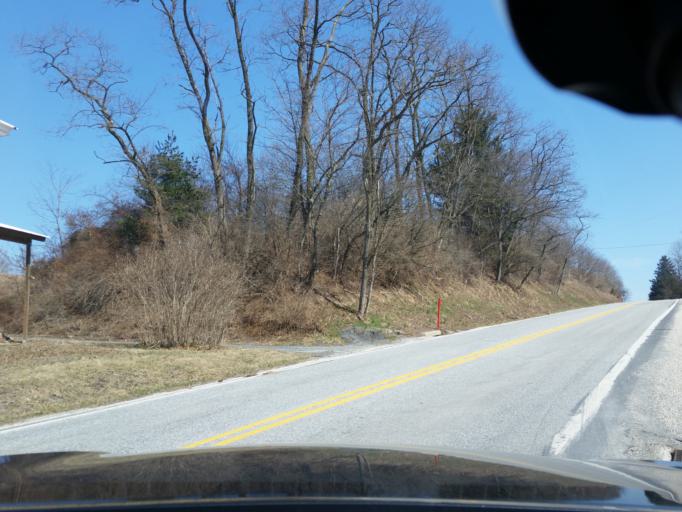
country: US
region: Pennsylvania
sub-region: Cumberland County
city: Schlusser
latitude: 40.3218
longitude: -77.1100
